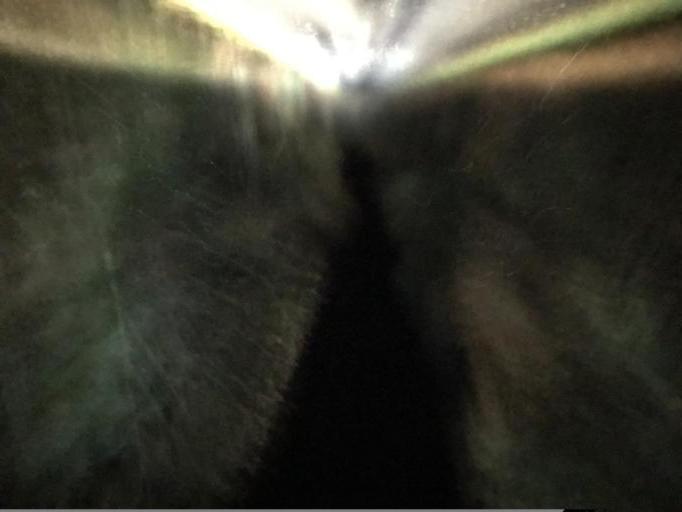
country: FR
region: Auvergne
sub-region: Departement de l'Allier
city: Saint-Yorre
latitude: 46.0571
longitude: 3.5145
